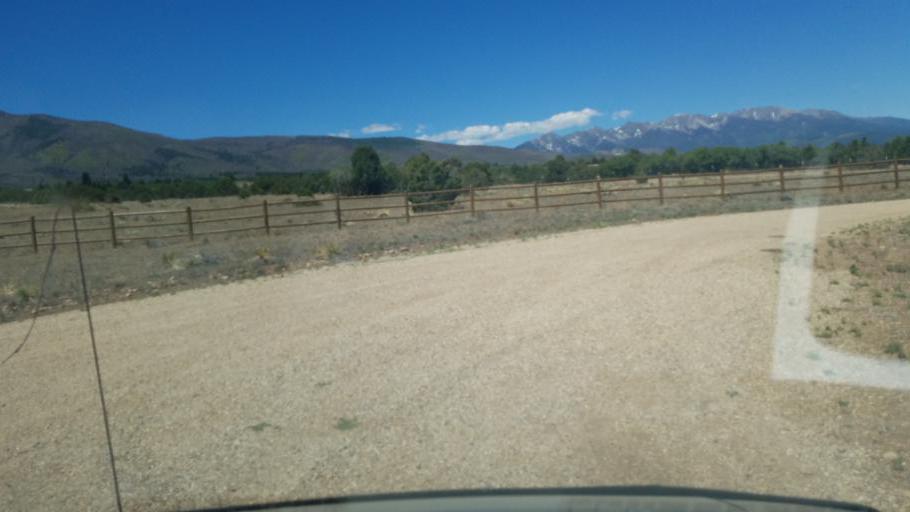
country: US
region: Colorado
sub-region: Custer County
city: Westcliffe
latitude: 38.2961
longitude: -105.6707
